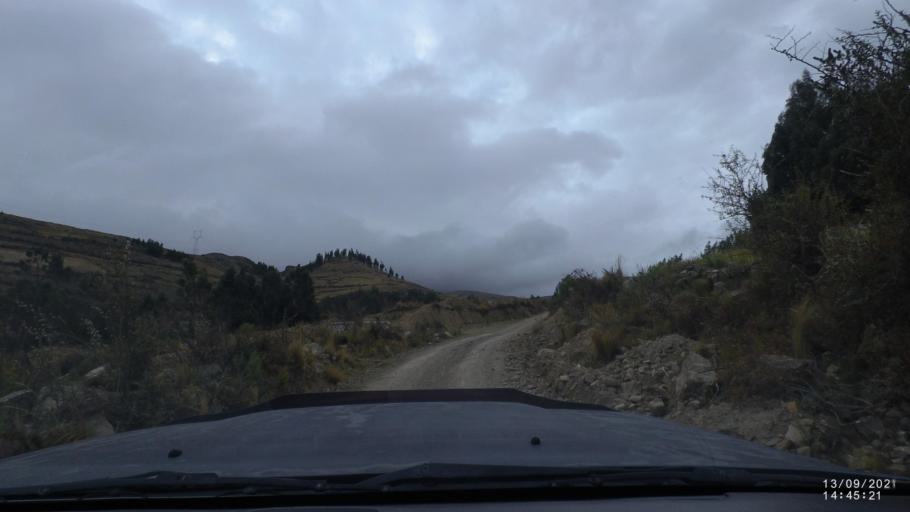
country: BO
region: Cochabamba
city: Colomi
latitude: -17.3538
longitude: -65.8091
